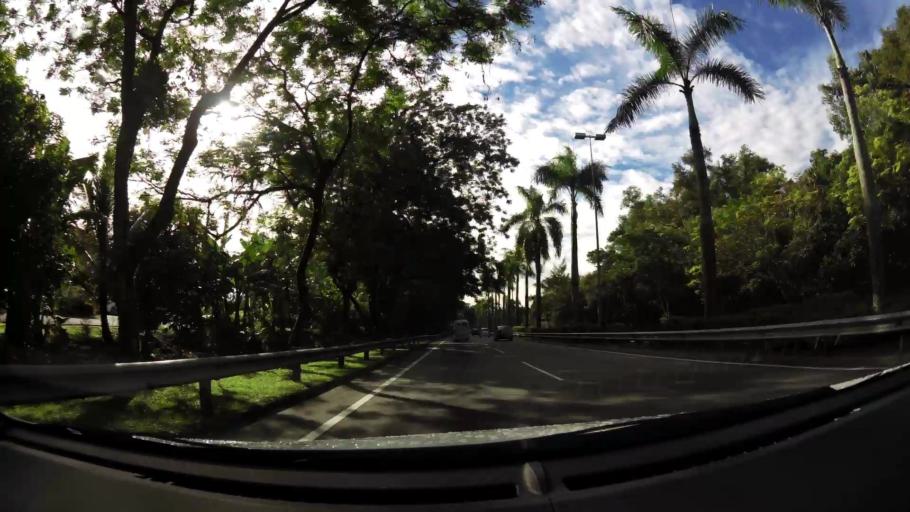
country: BN
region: Brunei and Muara
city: Bandar Seri Begawan
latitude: 4.8953
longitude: 114.9260
